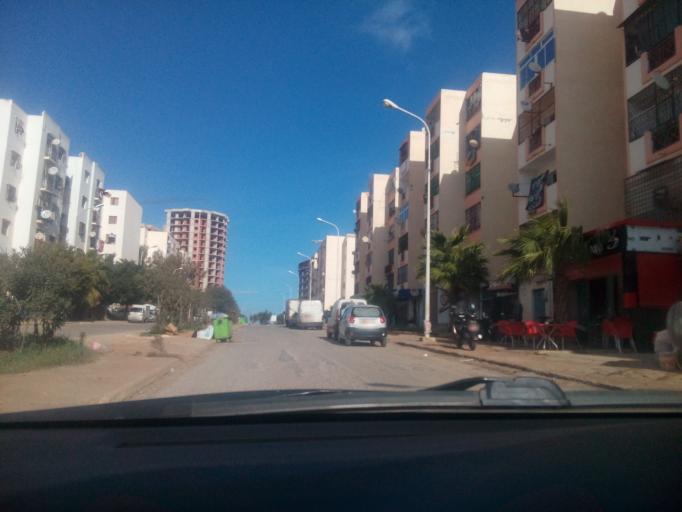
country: DZ
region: Oran
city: Bir el Djir
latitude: 35.7065
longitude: -0.5633
